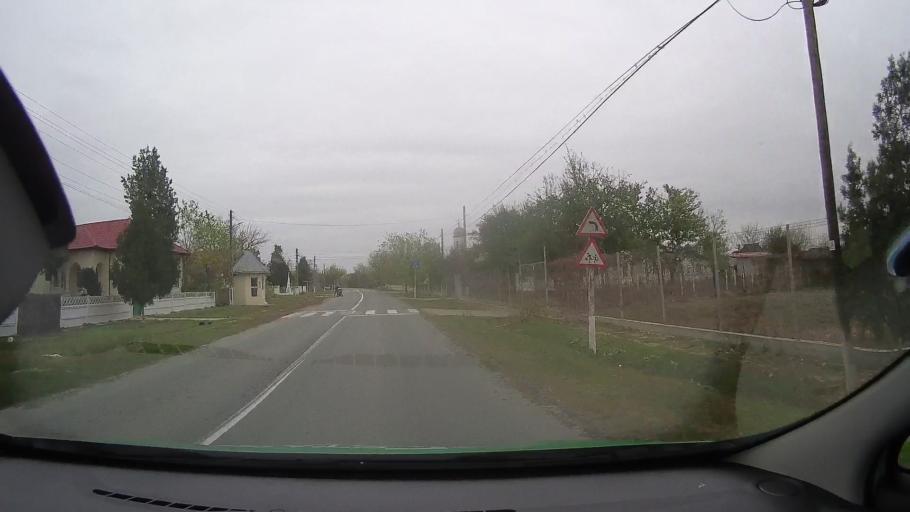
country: RO
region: Constanta
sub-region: Comuna Silistea
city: Silistea
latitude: 44.4455
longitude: 28.2379
